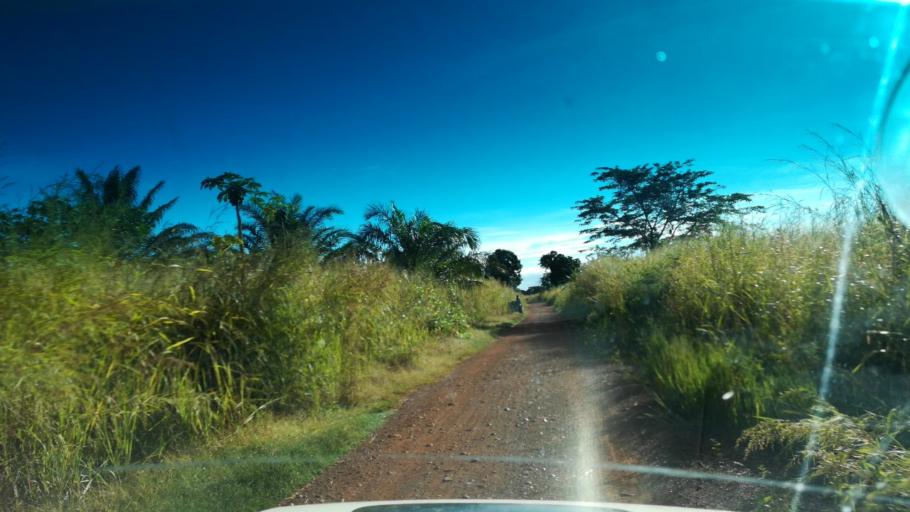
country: ZM
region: Northern
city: Kaputa
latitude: -8.3791
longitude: 28.9571
